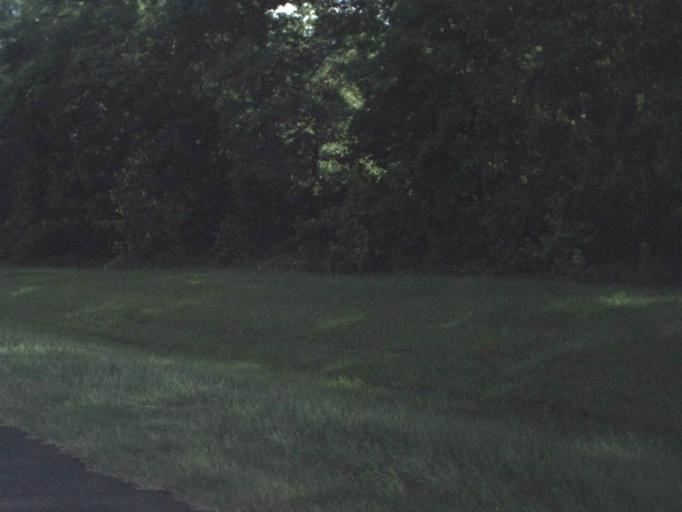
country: US
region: Florida
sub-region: Alachua County
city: Alachua
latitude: 29.7315
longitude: -82.3766
